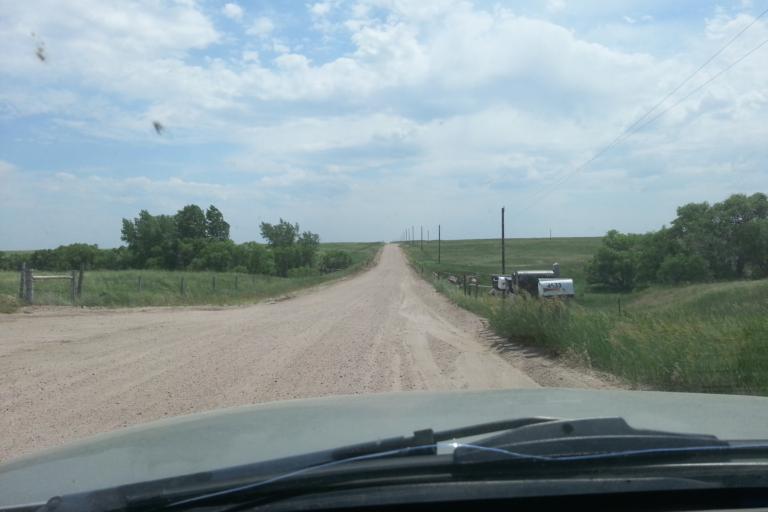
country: US
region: Wyoming
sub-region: Laramie County
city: Pine Bluffs
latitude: 41.0860
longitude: -104.4083
